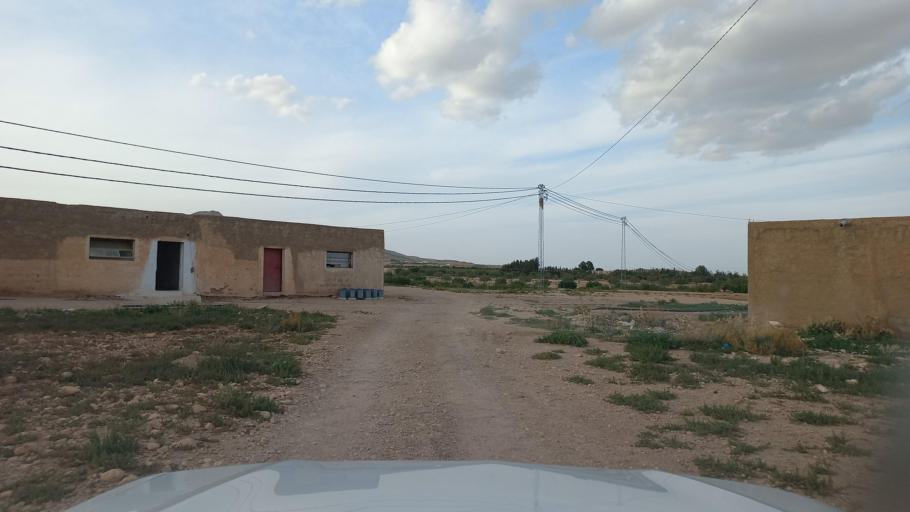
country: TN
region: Al Qasrayn
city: Sbiba
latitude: 35.4368
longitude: 9.0944
